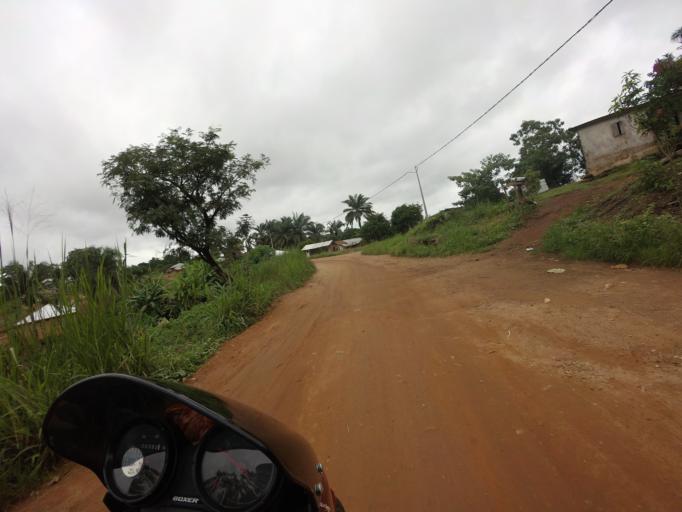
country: SL
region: Eastern Province
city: Koidu
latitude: 8.6440
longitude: -10.9333
